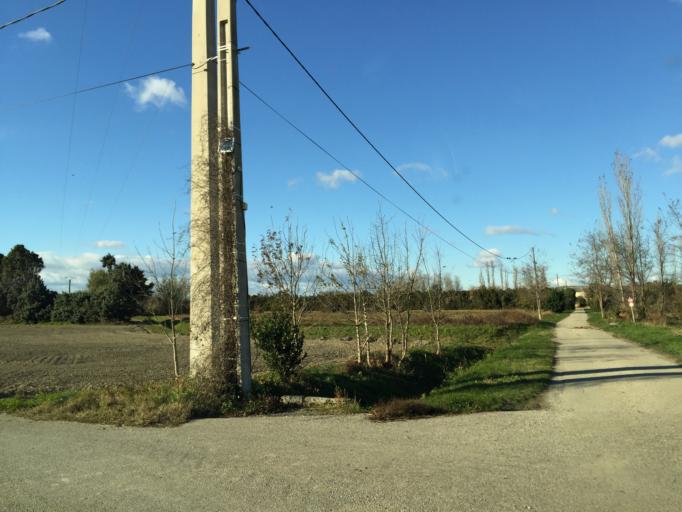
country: FR
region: Provence-Alpes-Cote d'Azur
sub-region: Departement du Vaucluse
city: Chateauneuf-du-Pape
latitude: 44.0325
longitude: 4.8281
